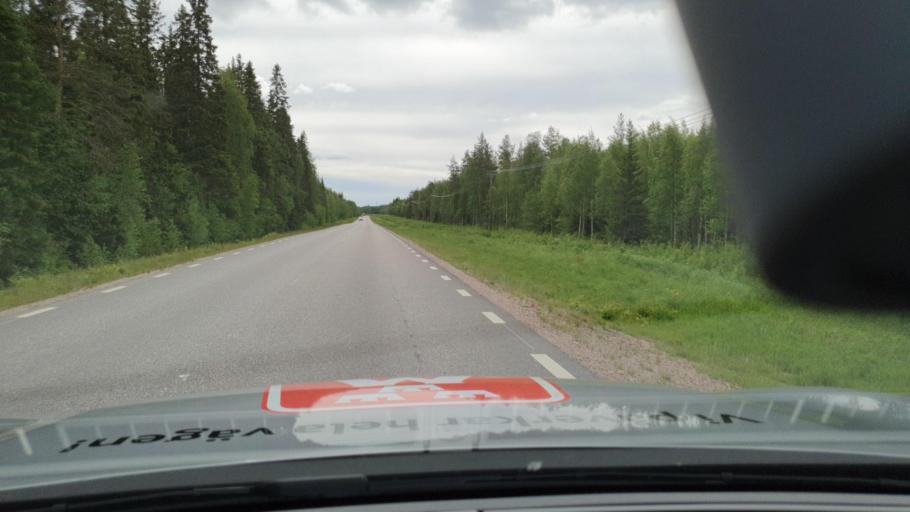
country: SE
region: Norrbotten
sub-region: Kalix Kommun
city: Kalix
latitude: 65.9091
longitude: 23.4555
